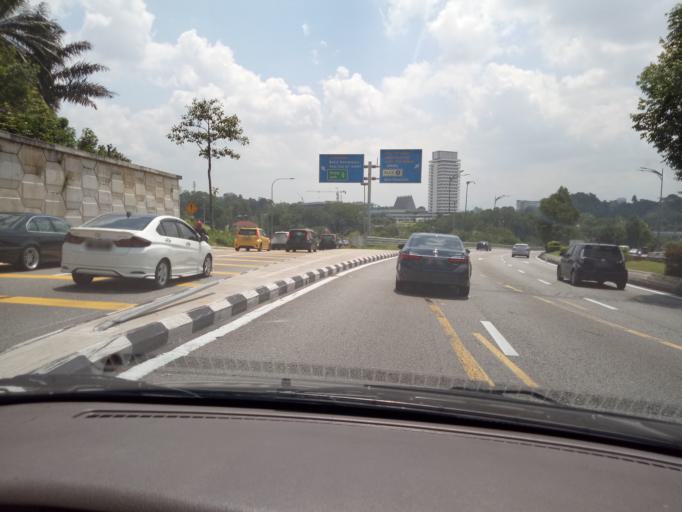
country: MY
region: Kuala Lumpur
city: Kuala Lumpur
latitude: 3.1444
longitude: 101.6783
